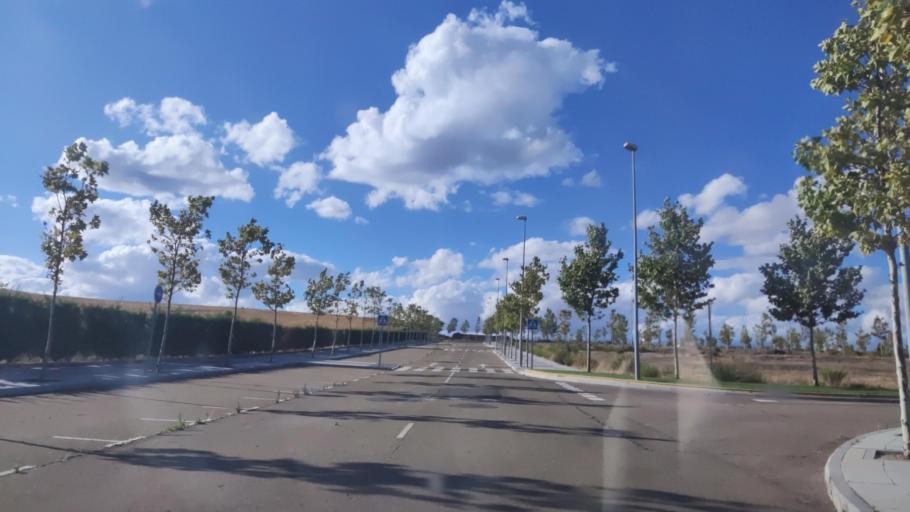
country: ES
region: Castille and Leon
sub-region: Provincia de Salamanca
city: Salamanca
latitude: 40.9656
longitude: -5.6925
